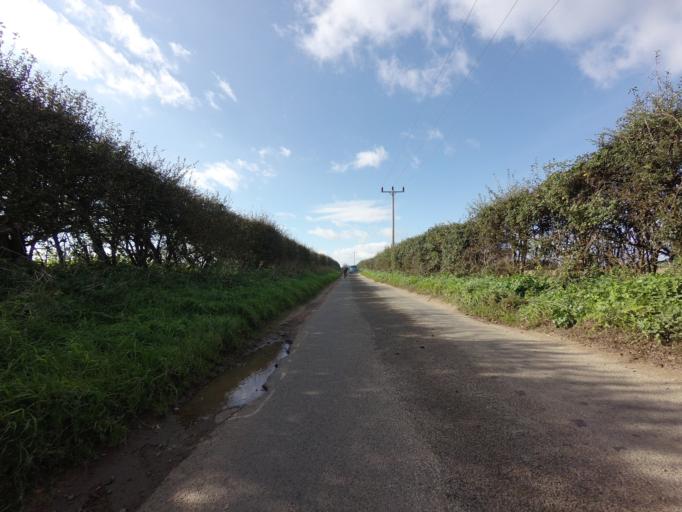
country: GB
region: England
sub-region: Norfolk
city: Hunstanton
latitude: 52.9360
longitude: 0.6142
